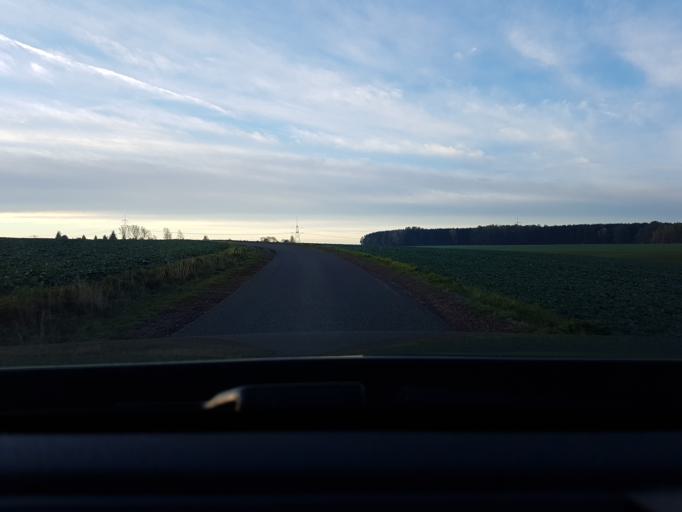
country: DE
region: Saxony
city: Altmittweida
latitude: 50.9580
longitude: 12.9684
